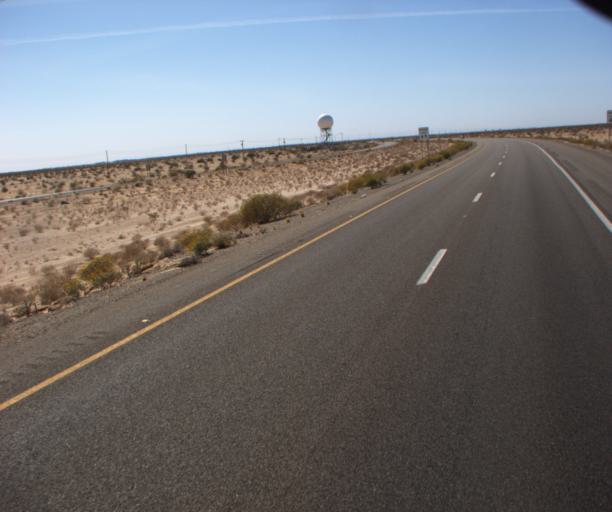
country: US
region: Arizona
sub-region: Yuma County
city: Somerton
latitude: 32.4967
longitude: -114.6521
